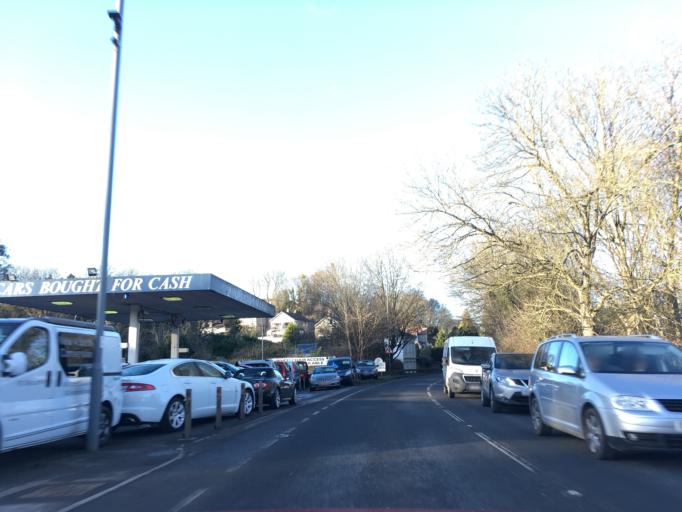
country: GB
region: England
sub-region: Bath and North East Somerset
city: Saltford
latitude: 51.3958
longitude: -2.4480
